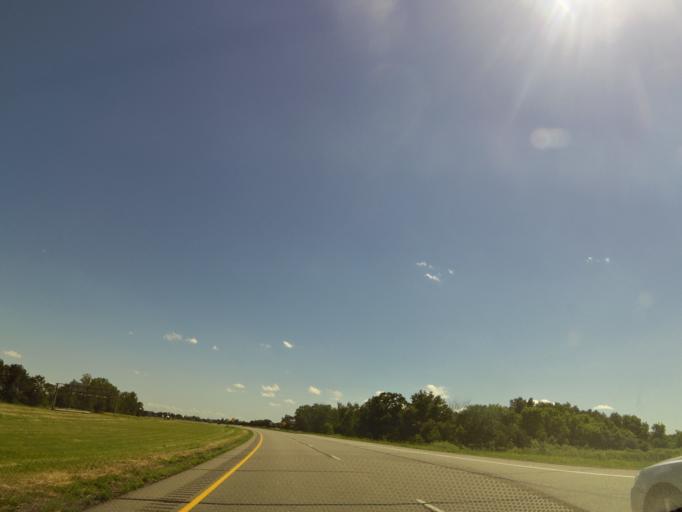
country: US
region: Minnesota
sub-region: Stearns County
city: Saint Augusta
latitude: 45.4919
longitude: -94.2457
